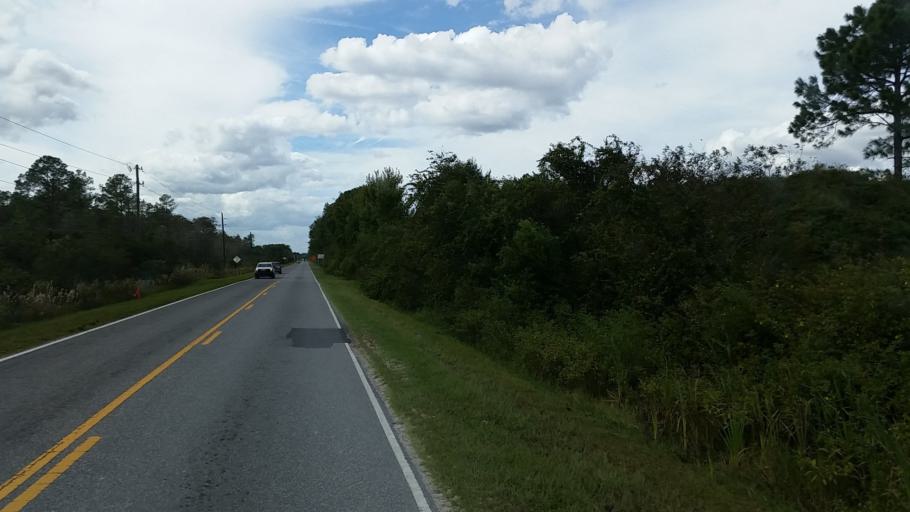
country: US
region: Florida
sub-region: Lake County
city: Four Corners
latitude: 28.3765
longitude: -81.7970
